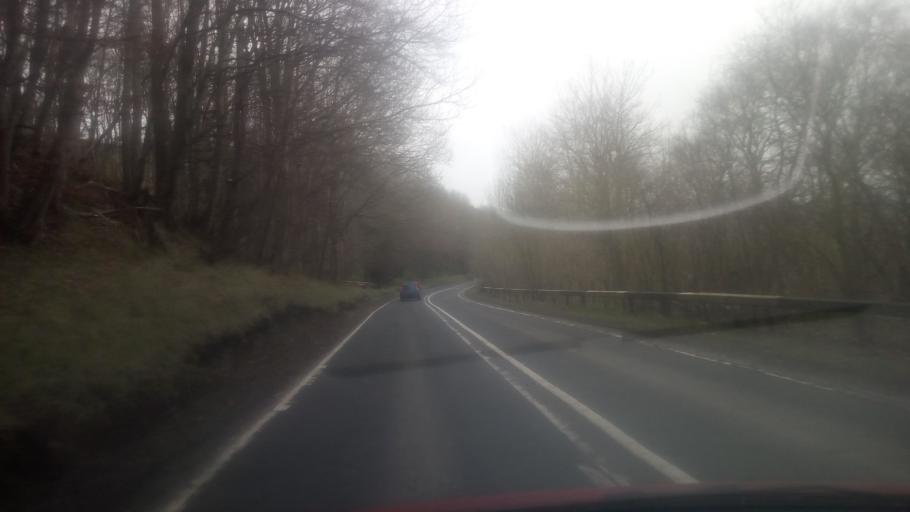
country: GB
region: Scotland
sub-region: The Scottish Borders
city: Galashiels
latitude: 55.6765
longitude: -2.8658
